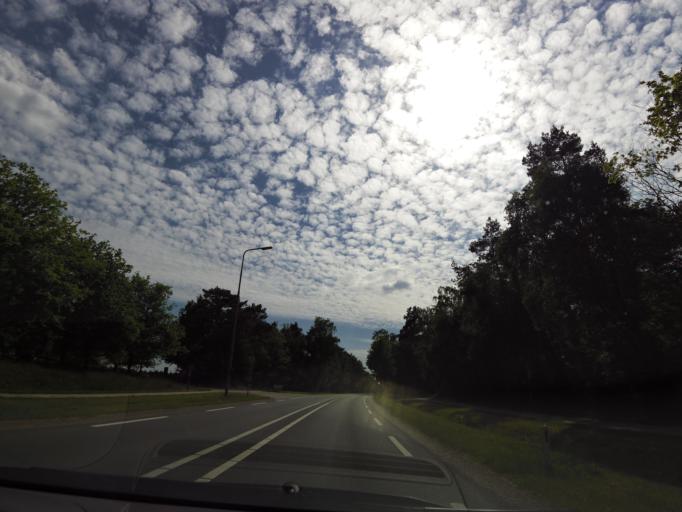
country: DE
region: North Rhine-Westphalia
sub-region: Regierungsbezirk Koln
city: Waldfeucht
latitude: 51.0956
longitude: 5.9982
